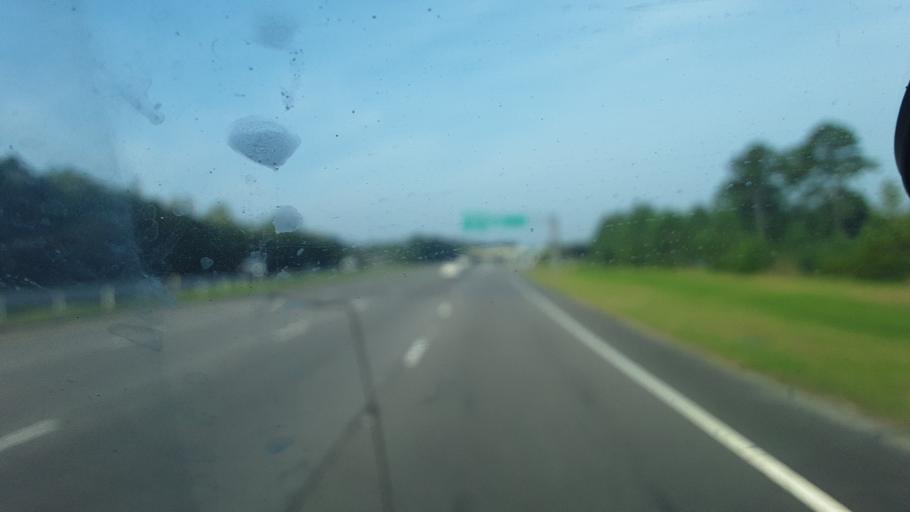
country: US
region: South Carolina
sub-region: Horry County
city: Myrtle Beach
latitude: 33.7568
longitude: -78.8475
